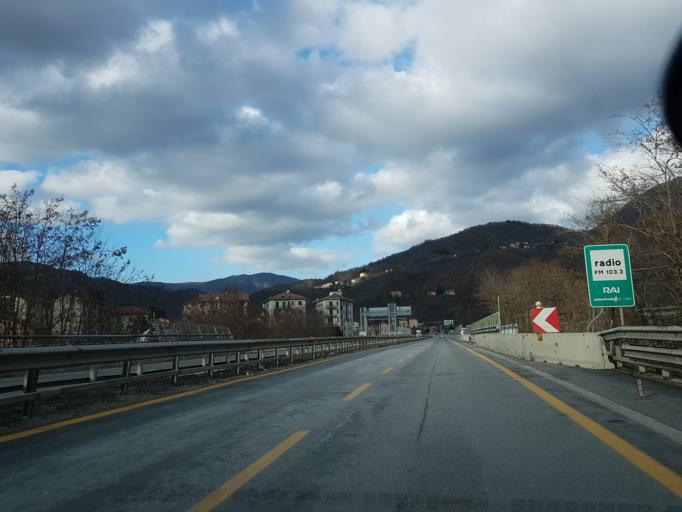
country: IT
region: Liguria
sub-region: Provincia di Genova
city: Ronco Scrivia
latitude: 44.6078
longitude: 8.9570
